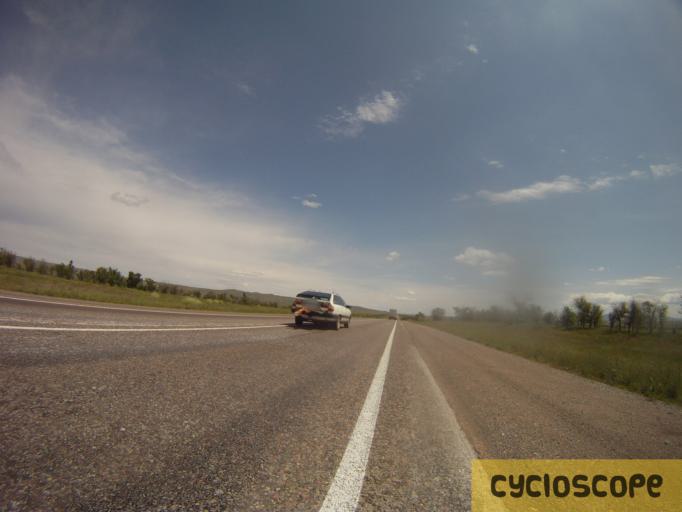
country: KZ
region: Zhambyl
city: Georgiyevka
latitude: 43.3074
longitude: 74.9063
